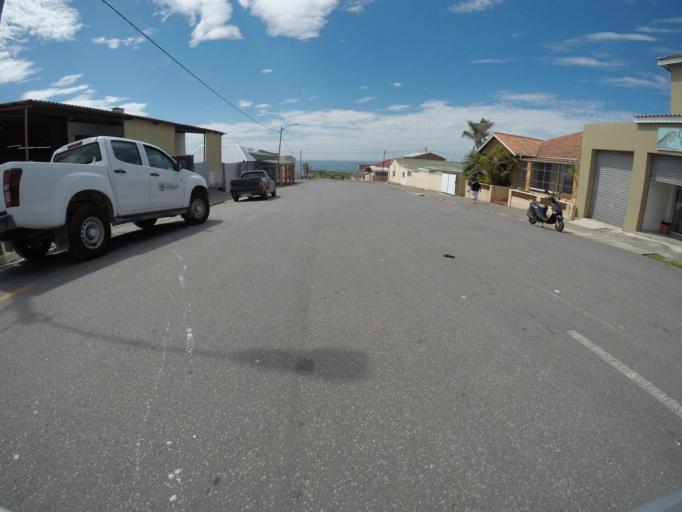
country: ZA
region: Eastern Cape
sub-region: Buffalo City Metropolitan Municipality
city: East London
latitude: -33.0325
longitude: 27.9079
